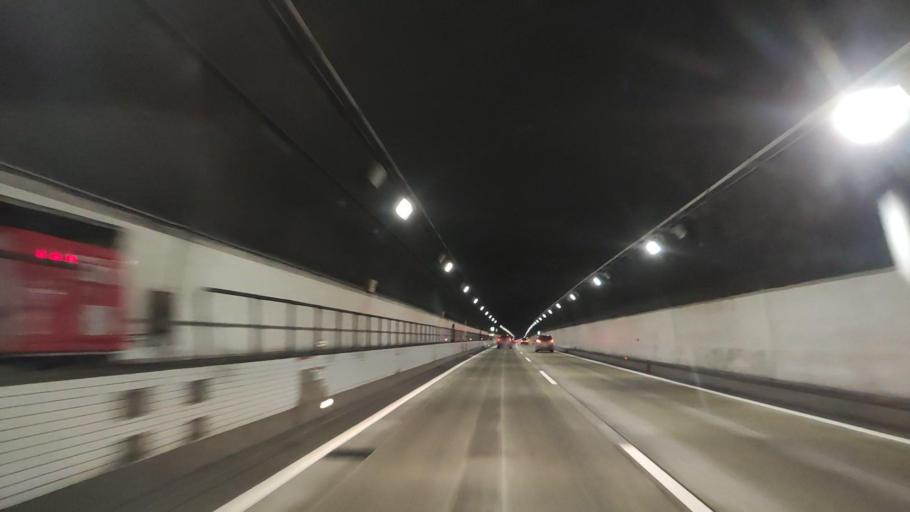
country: JP
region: Hiroshima
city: Shin'ichi
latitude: 34.4761
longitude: 133.2743
